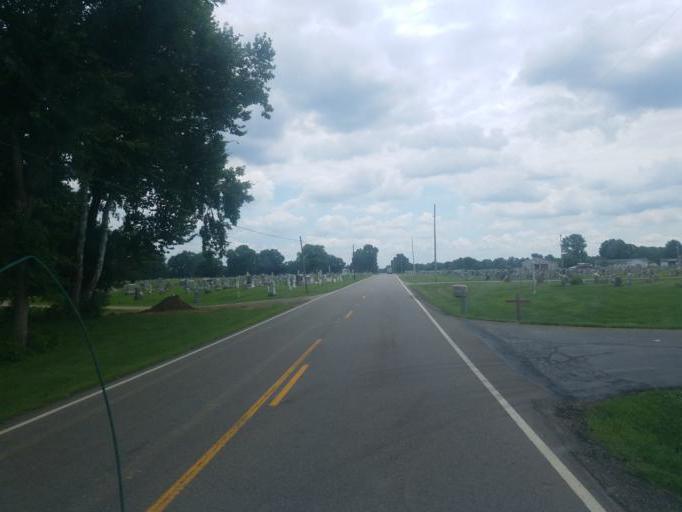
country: US
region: Ohio
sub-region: Licking County
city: Newark
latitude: 40.1224
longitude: -82.4341
